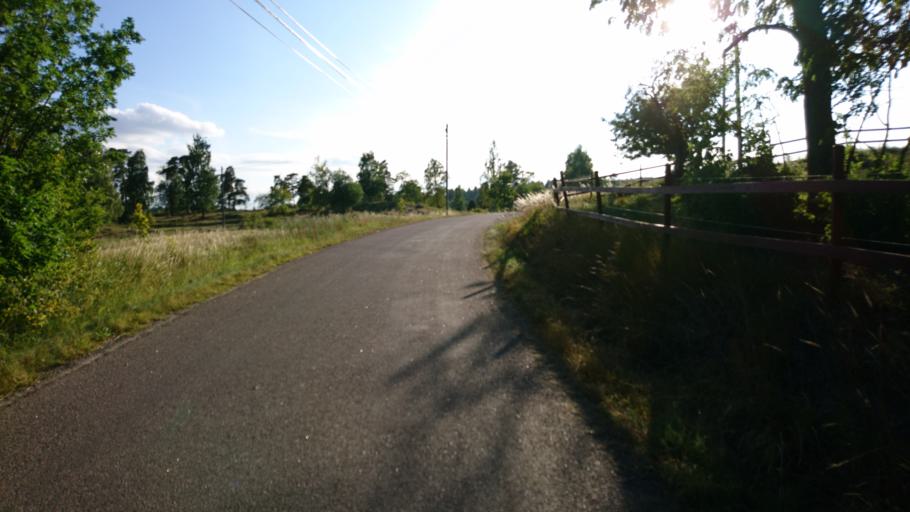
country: SE
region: Soedermanland
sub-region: Strangnas Kommun
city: Stallarholmen
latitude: 59.4020
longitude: 17.2954
